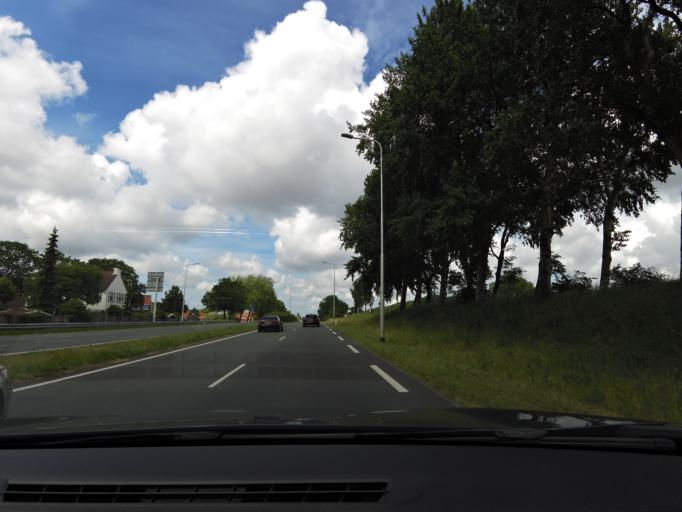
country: NL
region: Zeeland
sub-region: Gemeente Vlissingen
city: Vlissingen
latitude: 51.4640
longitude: 3.5929
